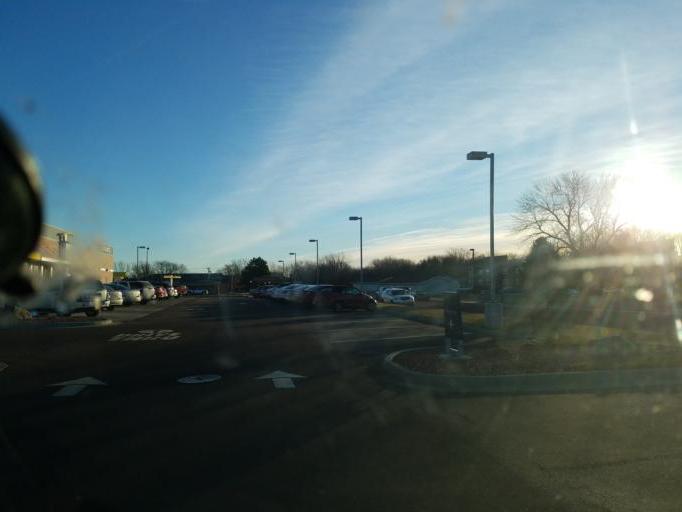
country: US
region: South Dakota
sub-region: Davison County
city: Mitchell
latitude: 43.7259
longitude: -98.0256
